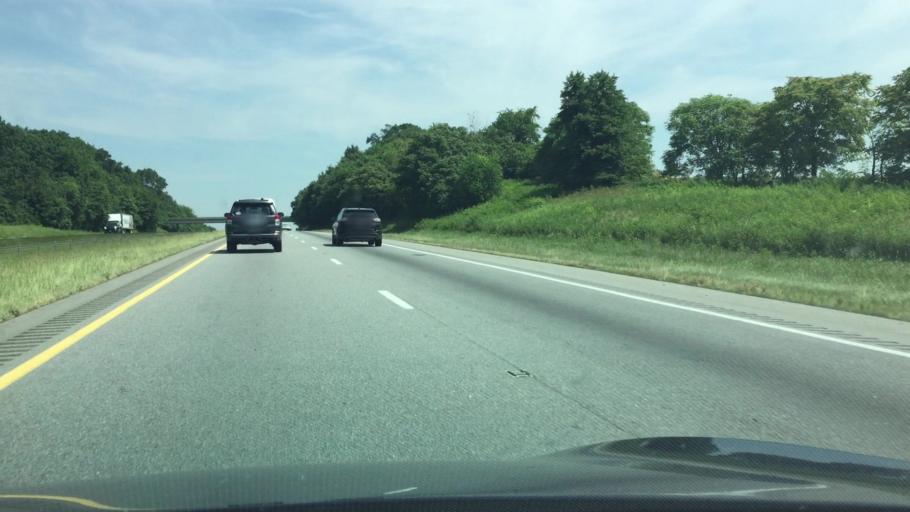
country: US
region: North Carolina
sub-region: Yadkin County
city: Jonesville
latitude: 36.0650
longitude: -80.8222
